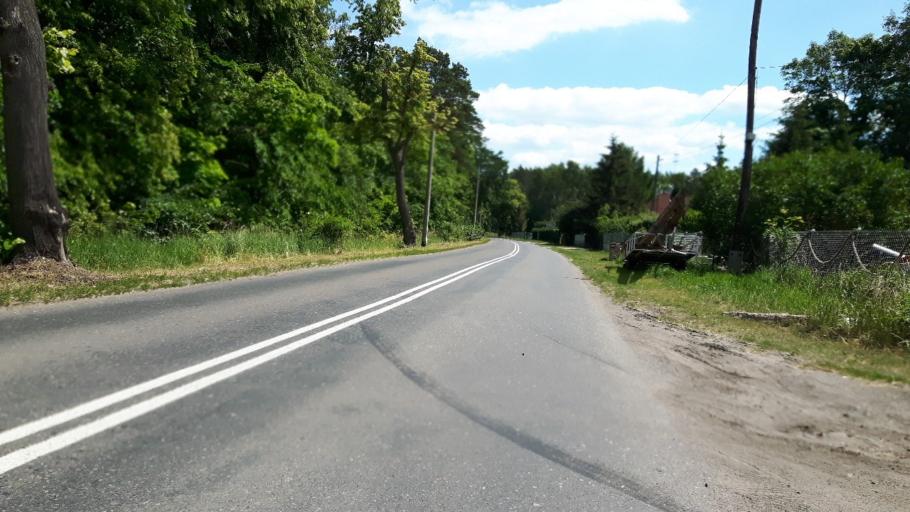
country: PL
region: Pomeranian Voivodeship
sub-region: Powiat gdanski
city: Cedry Wielkie
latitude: 54.3412
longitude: 18.8750
